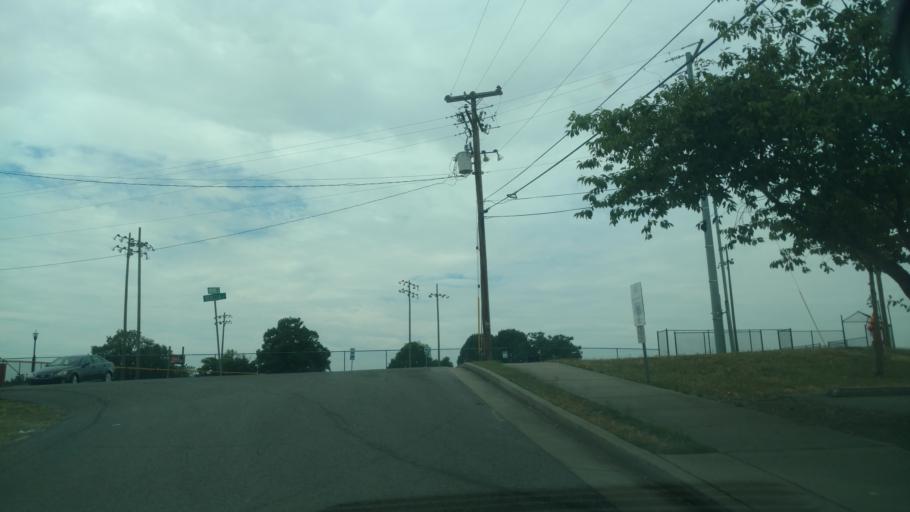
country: US
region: Tennessee
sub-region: Davidson County
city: Nashville
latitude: 36.1967
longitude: -86.7268
